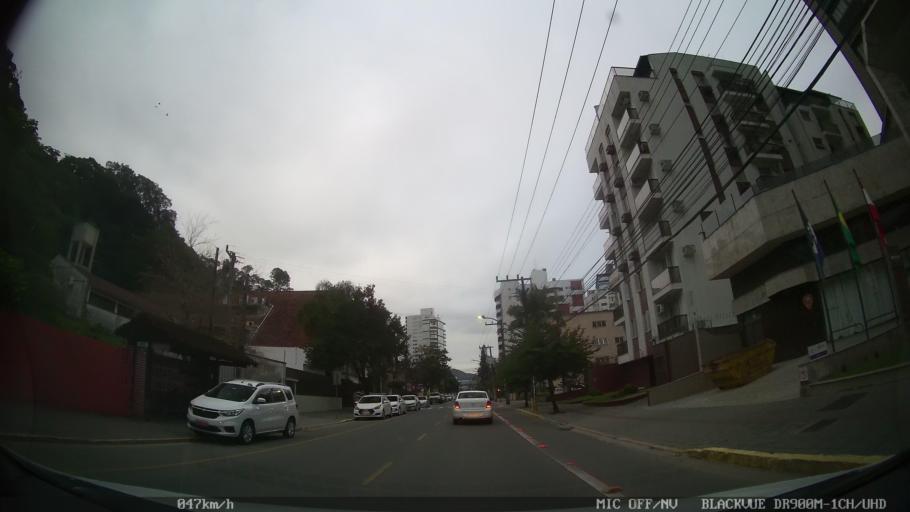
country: BR
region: Santa Catarina
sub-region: Joinville
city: Joinville
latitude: -26.3025
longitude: -48.8556
